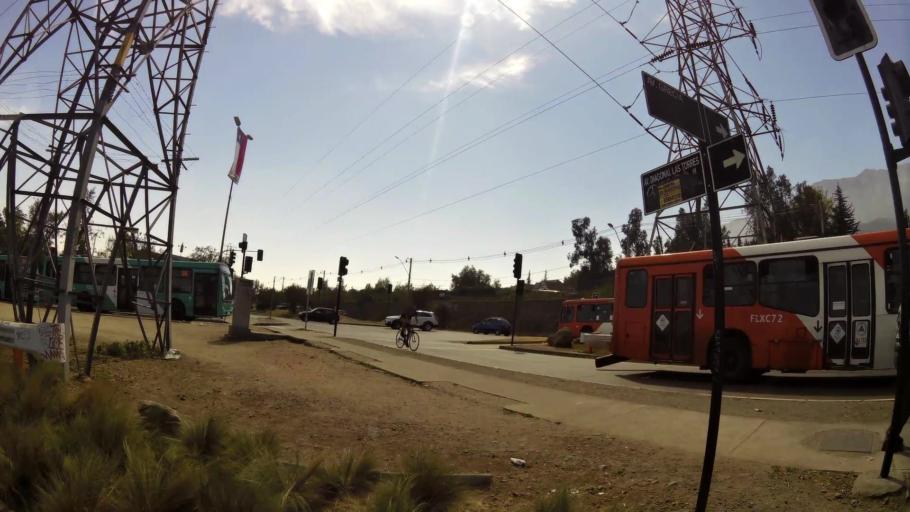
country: CL
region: Santiago Metropolitan
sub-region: Provincia de Santiago
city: Villa Presidente Frei, Nunoa, Santiago, Chile
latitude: -33.4798
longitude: -70.5244
